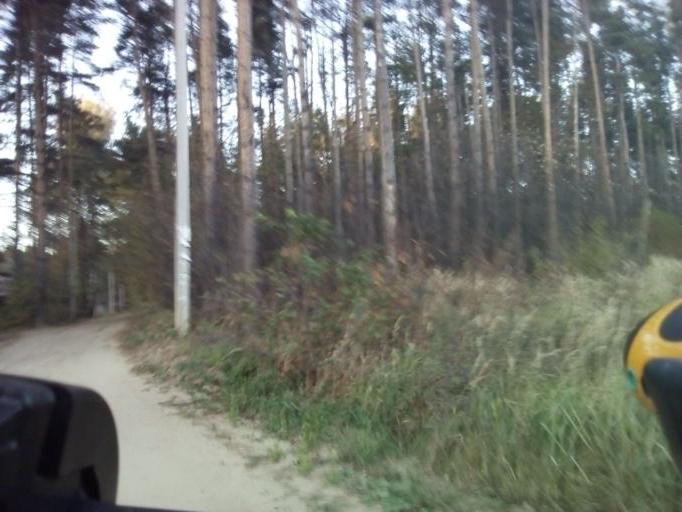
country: RU
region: Moskovskaya
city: Ramenskoye
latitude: 55.5867
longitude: 38.2297
